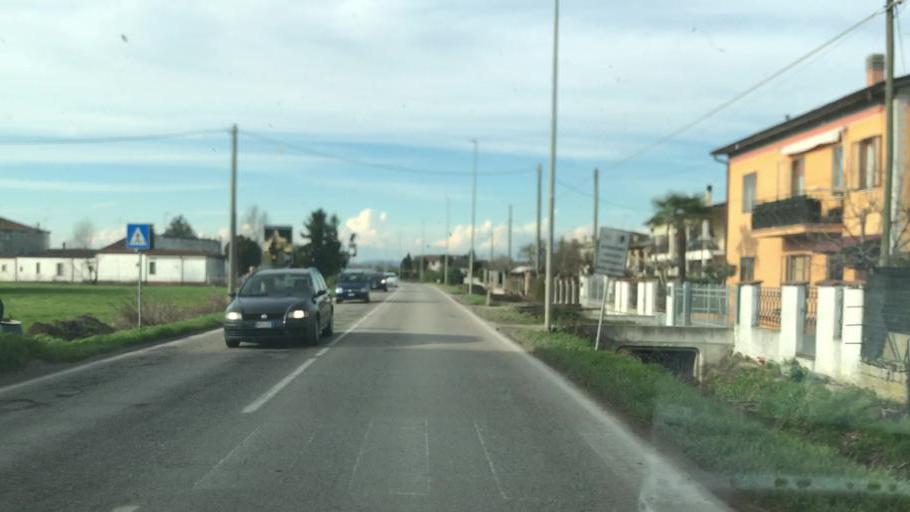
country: IT
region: Lombardy
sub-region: Provincia di Mantova
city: Cerlongo
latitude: 45.2780
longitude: 10.6592
